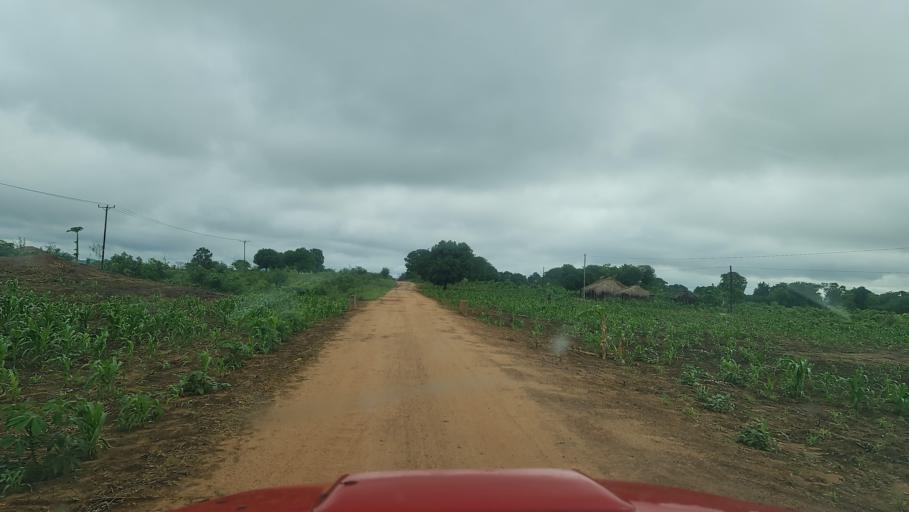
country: MW
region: Southern Region
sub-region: Nsanje District
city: Nsanje
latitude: -17.1971
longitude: 35.8433
